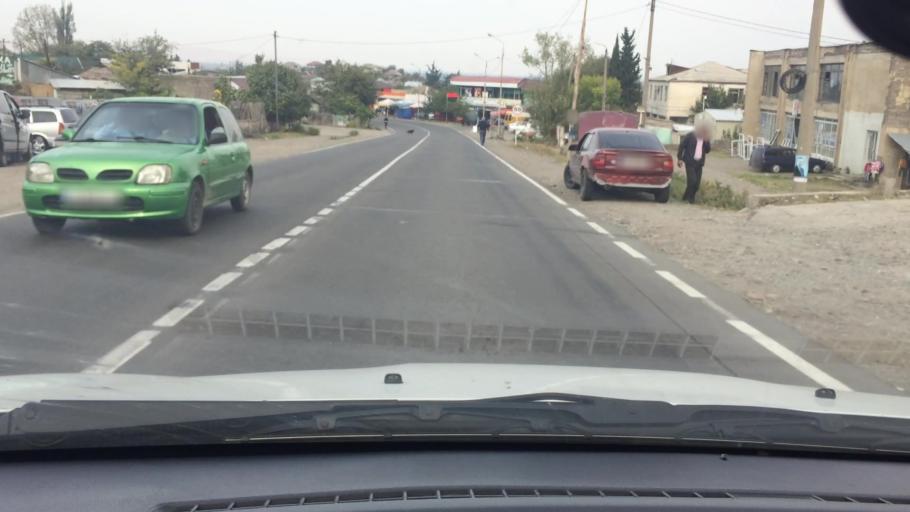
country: GE
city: Naghvarevi
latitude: 41.3650
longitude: 44.8390
